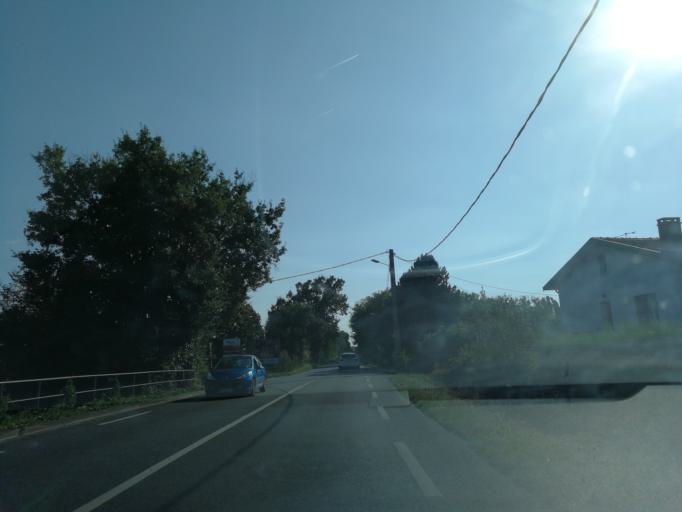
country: FR
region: Midi-Pyrenees
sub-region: Departement de la Haute-Garonne
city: Fonbeauzard
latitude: 43.6694
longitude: 1.4446
